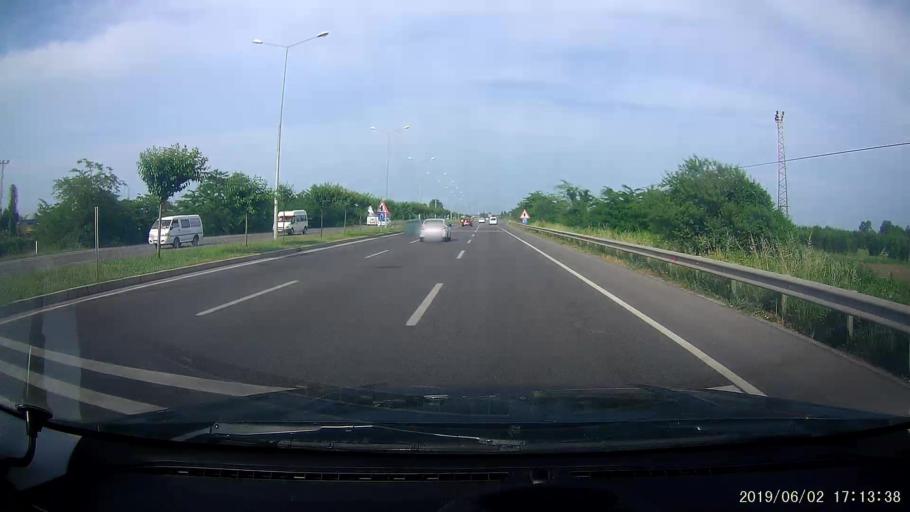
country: TR
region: Samsun
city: Tekkekoy
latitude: 41.2319
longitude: 36.5128
